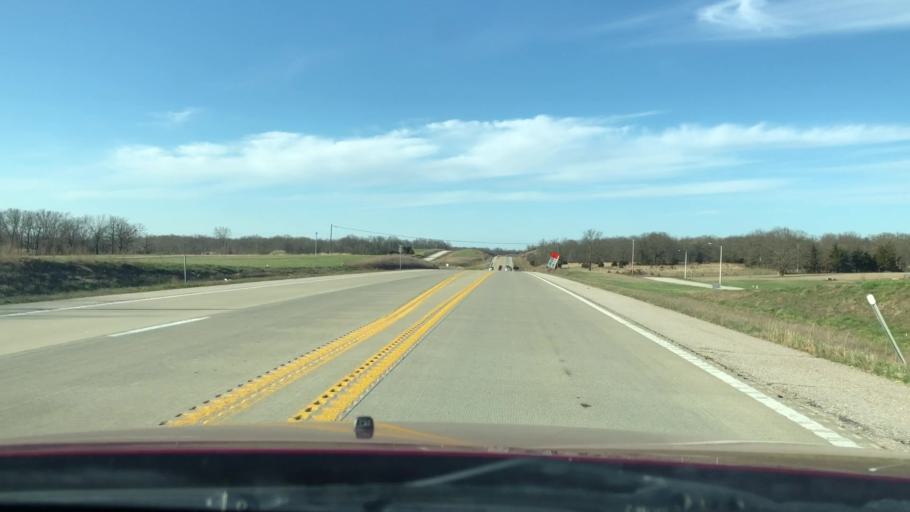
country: US
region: Missouri
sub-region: Camden County
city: Camdenton
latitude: 37.9496
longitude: -92.7155
